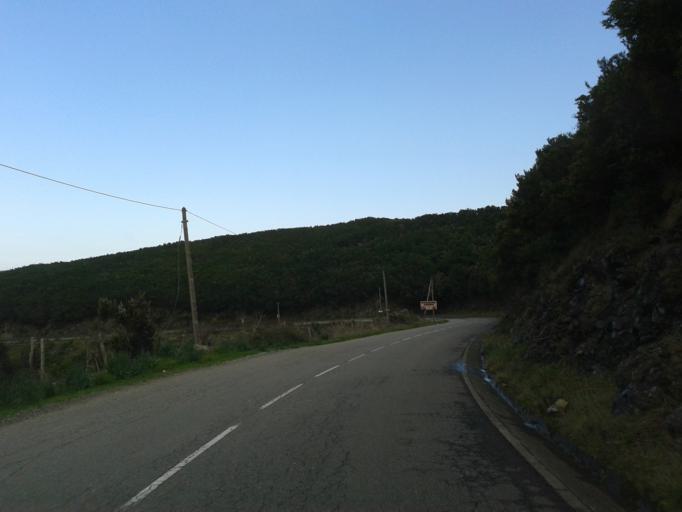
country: FR
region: Corsica
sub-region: Departement de la Haute-Corse
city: Biguglia
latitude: 42.5981
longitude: 9.4066
